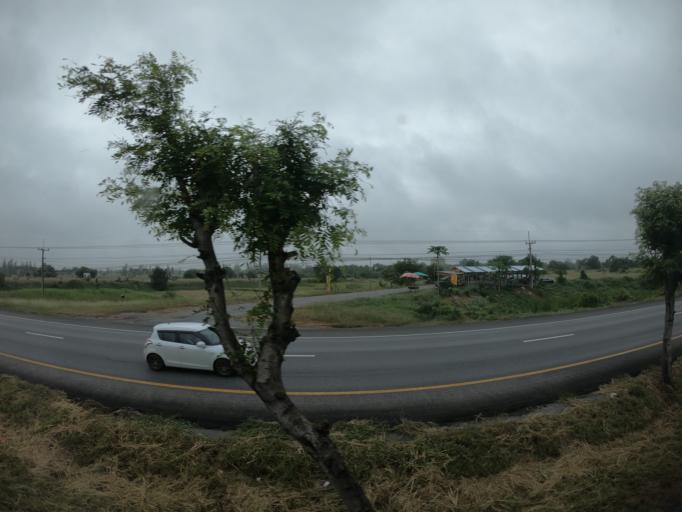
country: TH
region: Nakhon Ratchasima
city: Phimai
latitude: 15.3111
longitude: 102.4274
